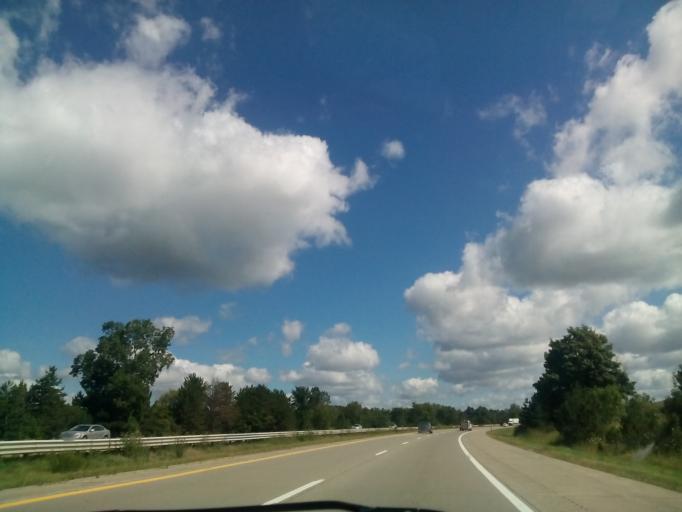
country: US
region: Michigan
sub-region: Genesee County
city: Lake Fenton
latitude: 42.8960
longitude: -83.7380
